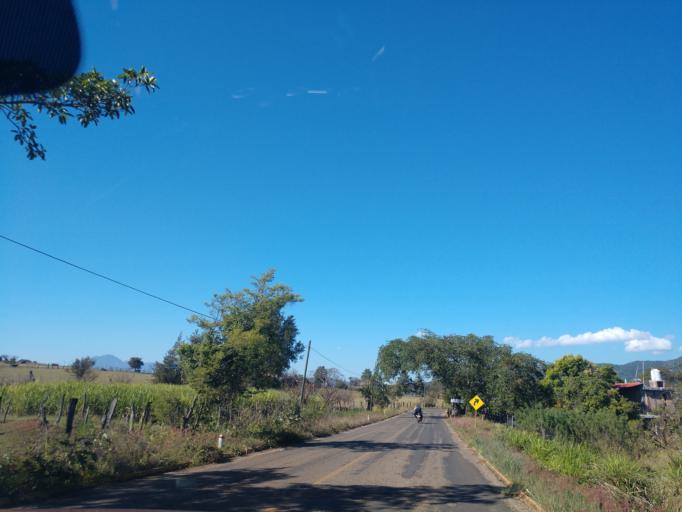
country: MX
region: Nayarit
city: Compostela
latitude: 21.2690
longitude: -104.8919
